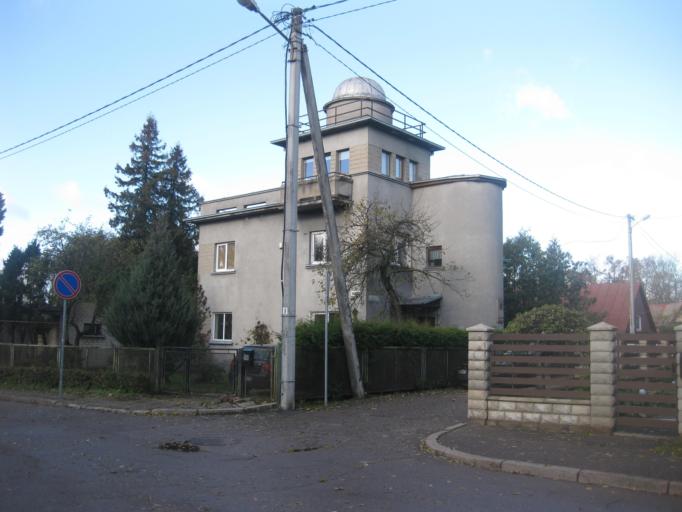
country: LT
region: Kauno apskritis
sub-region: Kaunas
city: Kaunas
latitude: 54.8999
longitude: 23.9272
